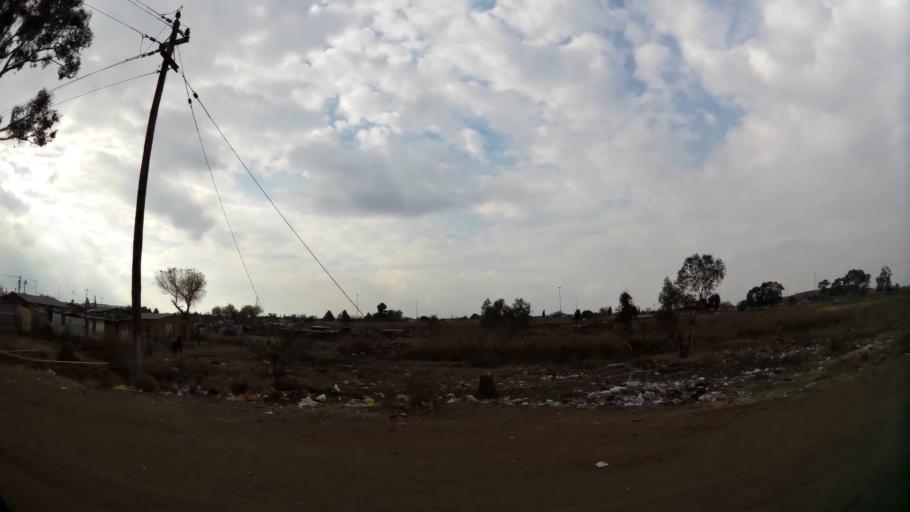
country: ZA
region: Gauteng
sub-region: Sedibeng District Municipality
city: Vanderbijlpark
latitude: -26.6703
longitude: 27.8456
